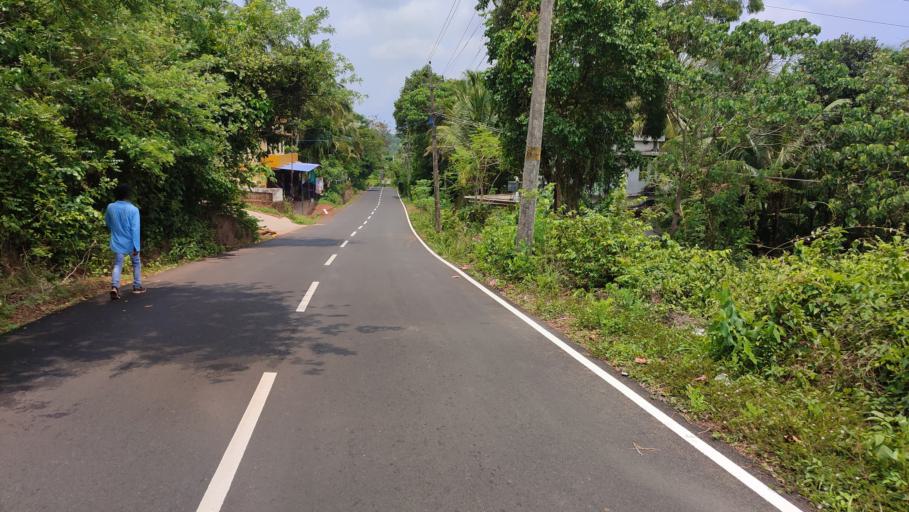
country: IN
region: Kerala
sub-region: Kasaragod District
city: Kannangad
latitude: 12.3221
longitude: 75.1347
